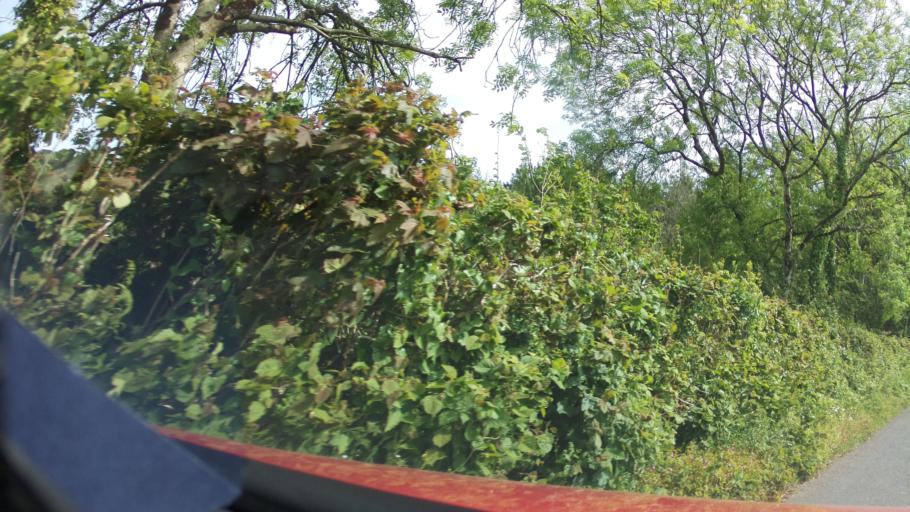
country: GB
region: England
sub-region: Devon
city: Kingsbridge
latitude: 50.3640
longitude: -3.7694
